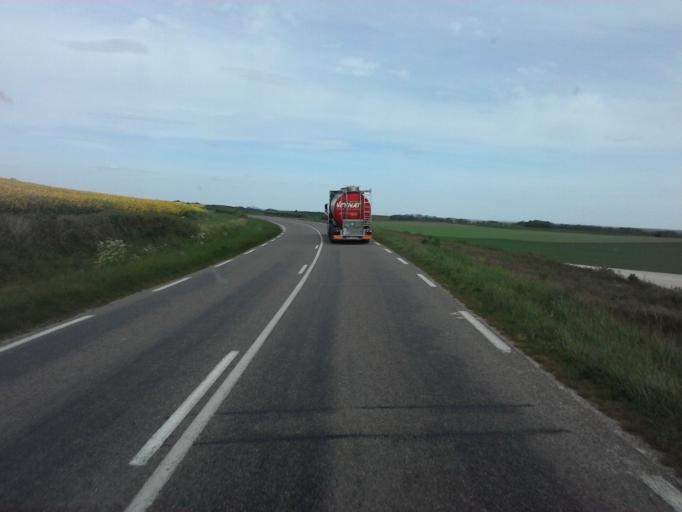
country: FR
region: Champagne-Ardenne
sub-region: Departement de l'Aube
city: Bouilly
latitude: 48.1358
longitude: 3.9960
